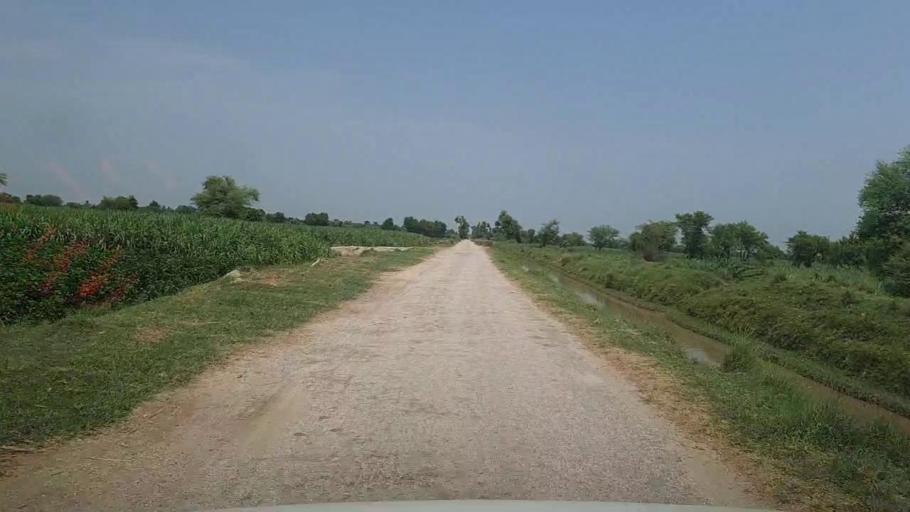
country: PK
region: Sindh
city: Karaundi
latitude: 26.8873
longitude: 68.3338
